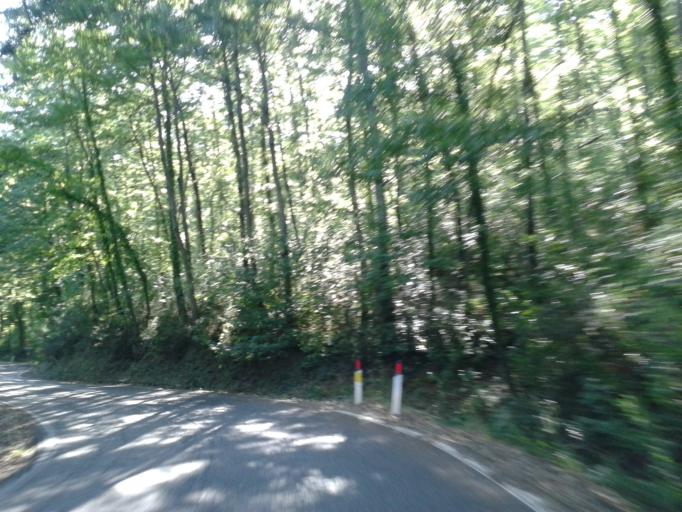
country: IT
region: Tuscany
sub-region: Province of Pisa
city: Chianni
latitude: 43.4469
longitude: 10.6224
